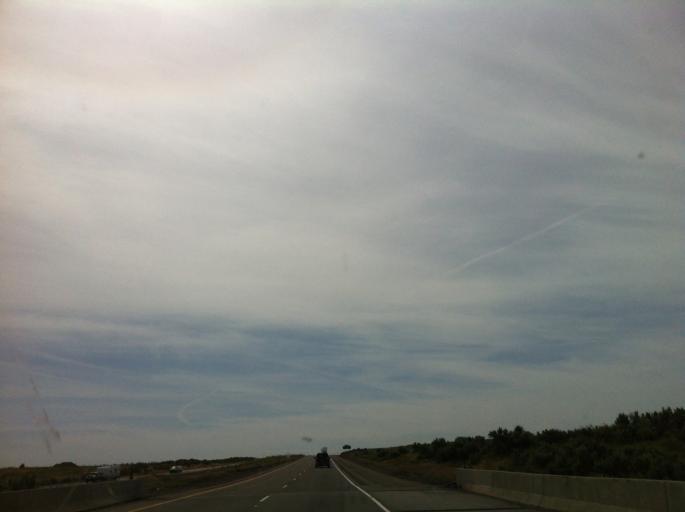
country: US
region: Oregon
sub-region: Malheur County
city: Ontario
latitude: 44.0978
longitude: -117.0371
